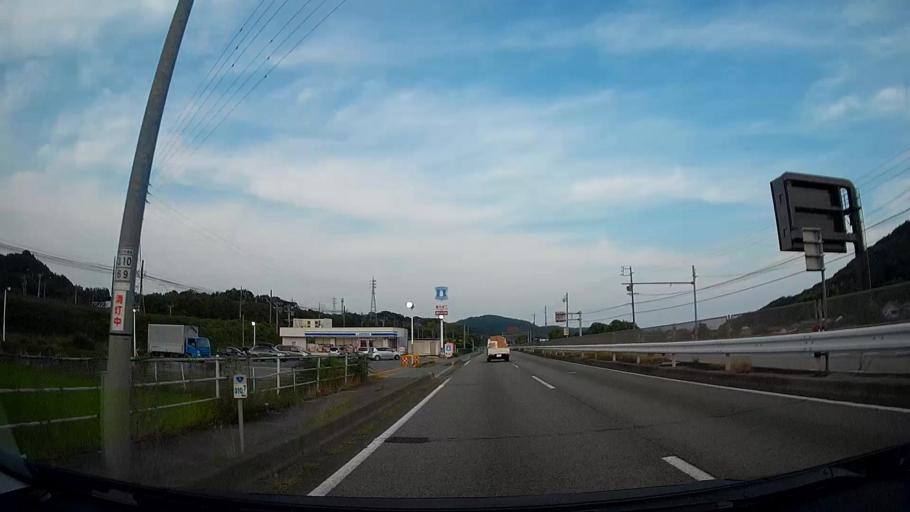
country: JP
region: Aichi
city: Gamagori
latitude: 34.8668
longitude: 137.2965
